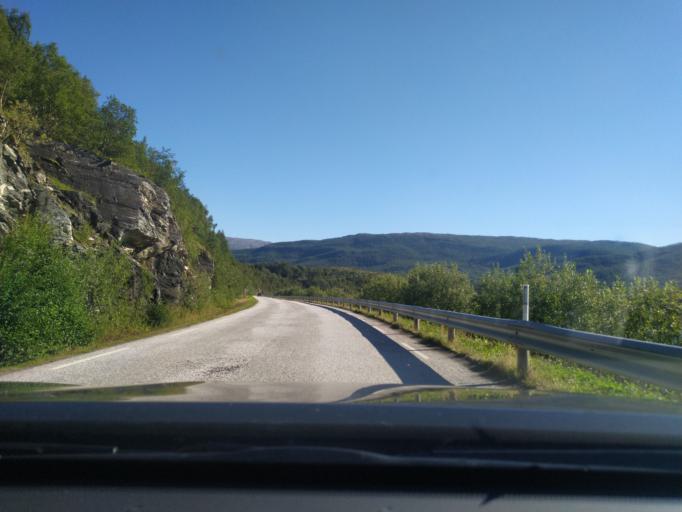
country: NO
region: Troms
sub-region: Dyroy
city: Brostadbotn
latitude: 68.9326
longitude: 17.6858
